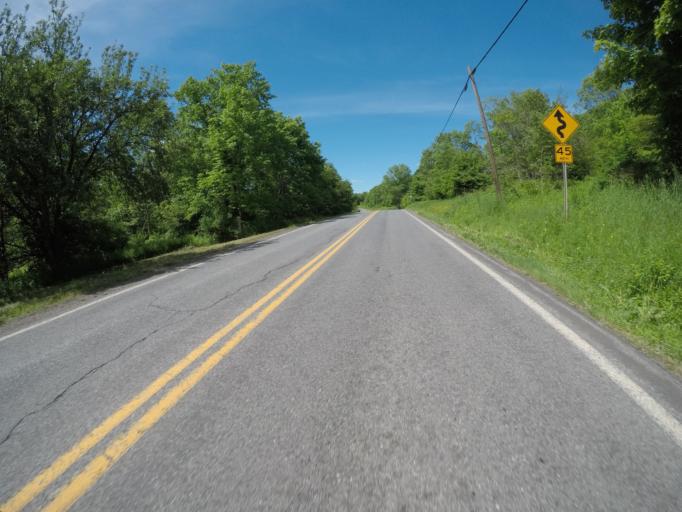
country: US
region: New York
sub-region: Delaware County
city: Delhi
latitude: 42.1529
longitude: -74.7977
